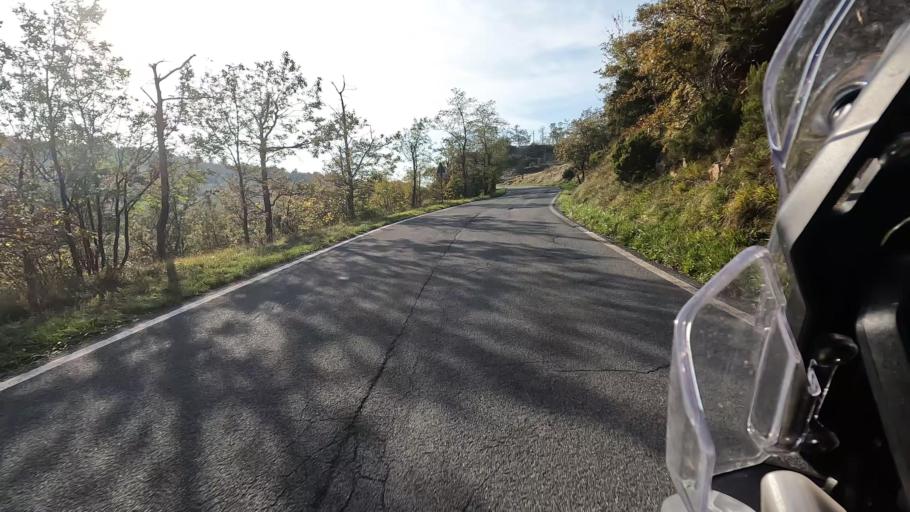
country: IT
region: Liguria
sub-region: Provincia di Savona
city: Urbe
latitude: 44.4767
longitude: 8.5669
